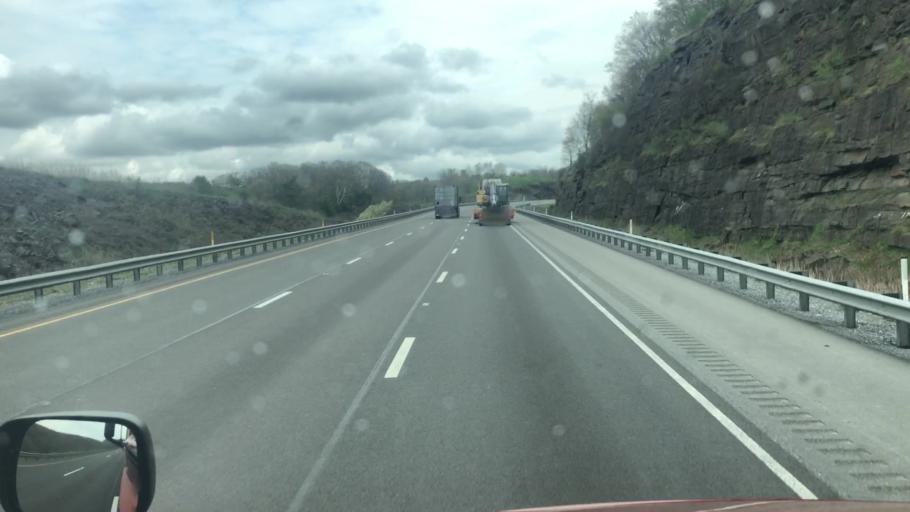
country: US
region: Pennsylvania
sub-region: Clinton County
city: Castanea
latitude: 41.0615
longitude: -77.3730
